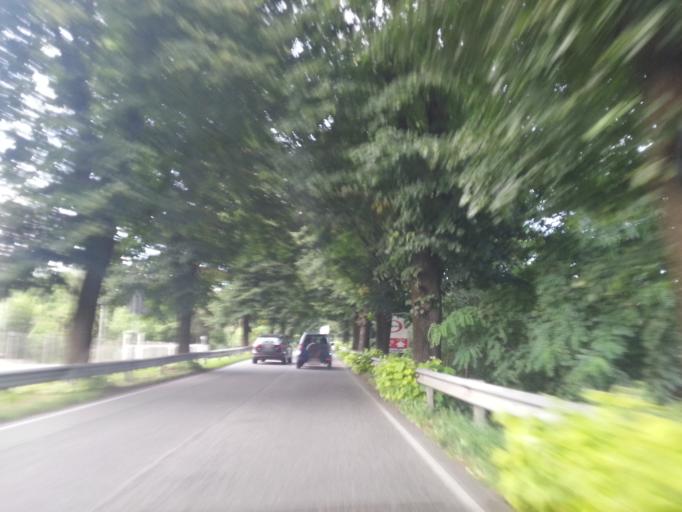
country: IT
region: Lombardy
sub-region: Provincia di Monza e Brianza
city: Besana in Brianza
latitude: 45.6976
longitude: 9.2793
